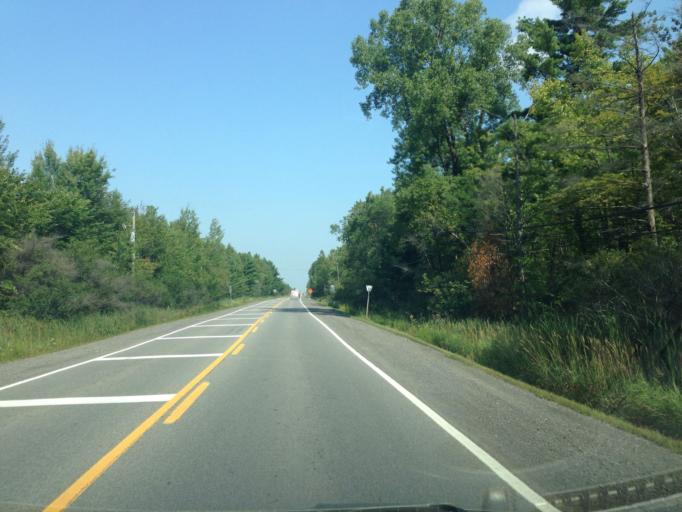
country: CA
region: Ontario
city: Ottawa
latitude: 45.3605
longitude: -75.5343
